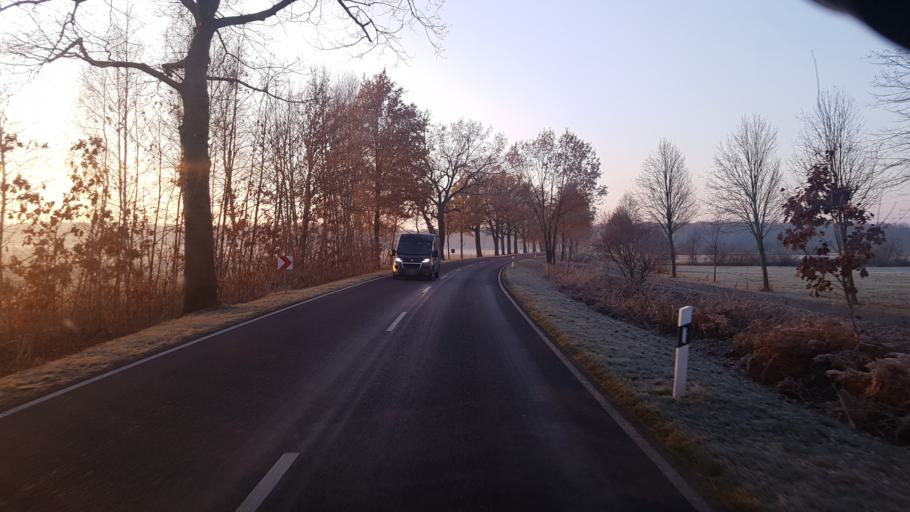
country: DE
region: Brandenburg
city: Tettau
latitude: 51.4542
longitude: 13.7389
